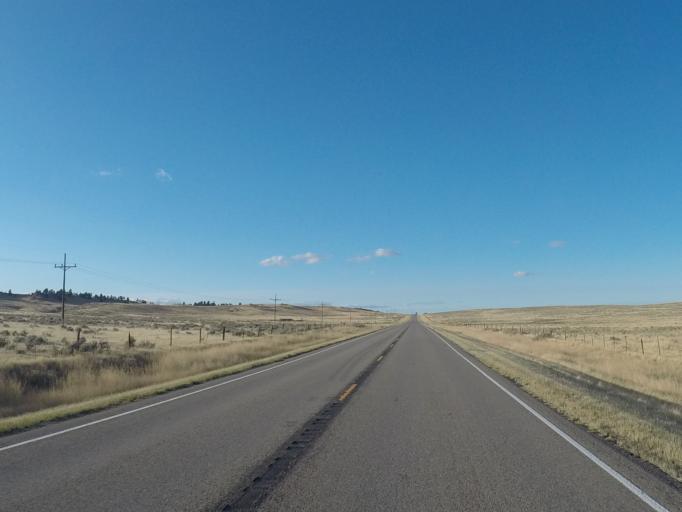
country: US
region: Montana
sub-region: Golden Valley County
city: Ryegate
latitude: 46.2305
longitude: -108.9317
